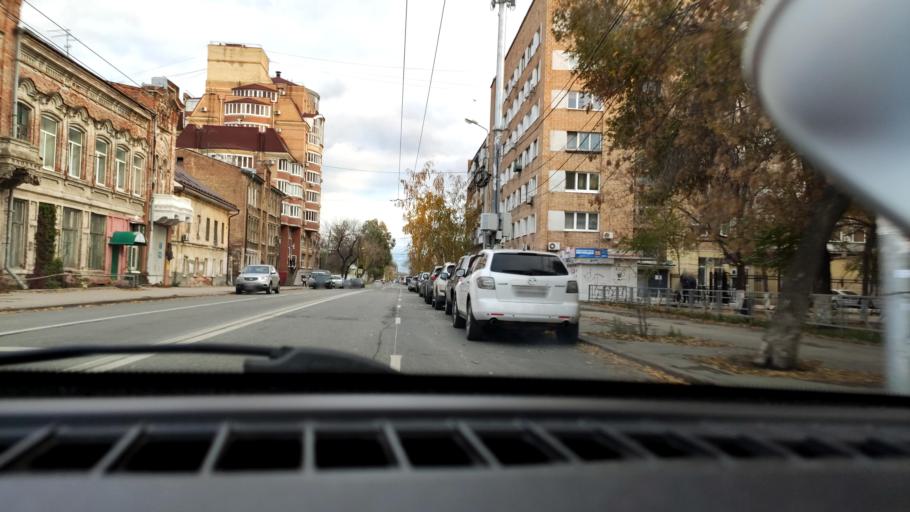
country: RU
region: Samara
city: Samara
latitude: 53.1848
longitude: 50.1022
